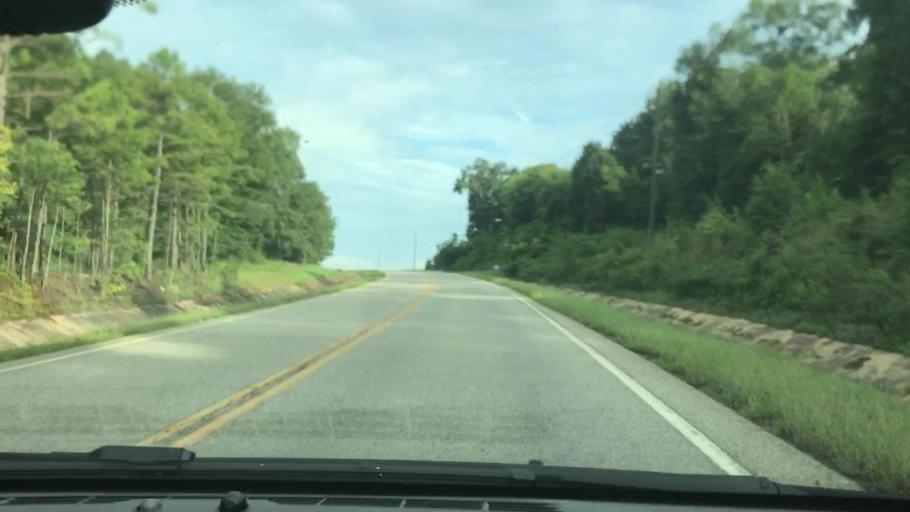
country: US
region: Georgia
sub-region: Quitman County
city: Georgetown
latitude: 31.7538
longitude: -85.0579
